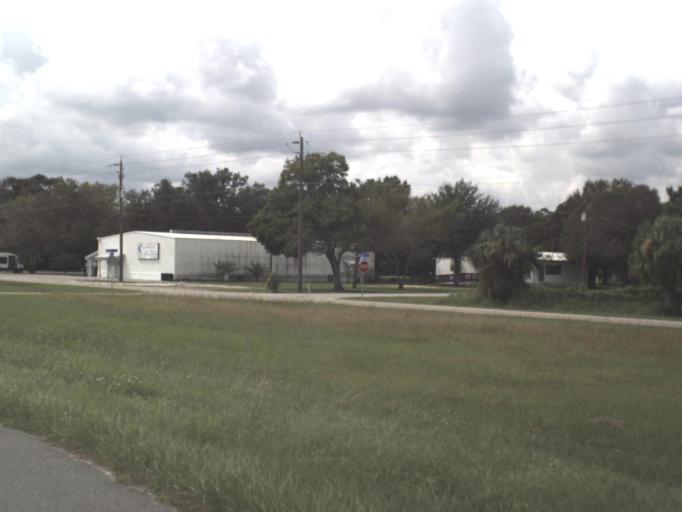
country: US
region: Florida
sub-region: Hendry County
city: LaBelle
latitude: 26.7822
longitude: -81.4375
